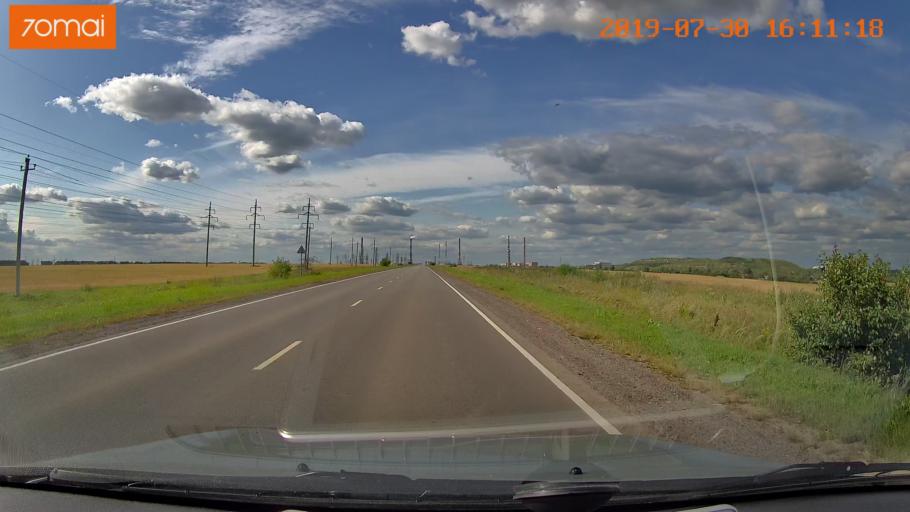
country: RU
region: Moskovskaya
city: Lopatinskiy
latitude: 55.2739
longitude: 38.7122
